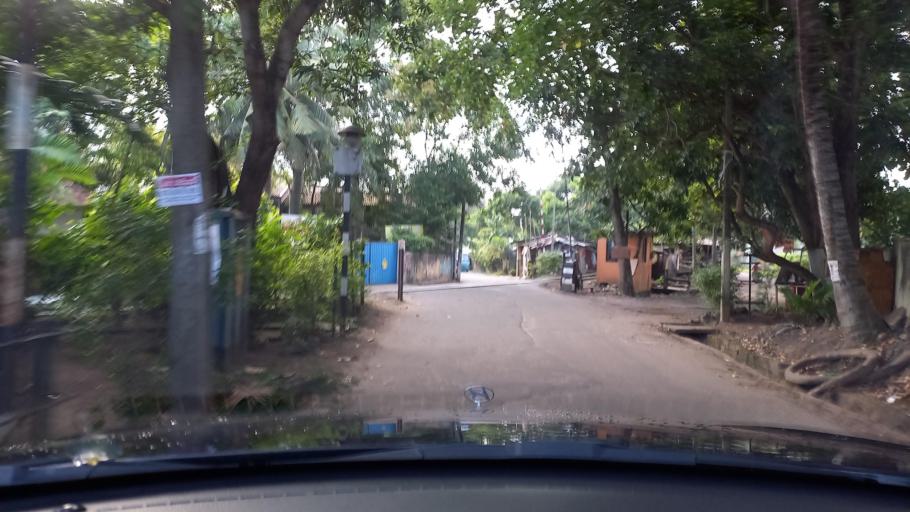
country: LK
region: Western
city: Pita Kotte
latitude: 6.8769
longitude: 79.8830
